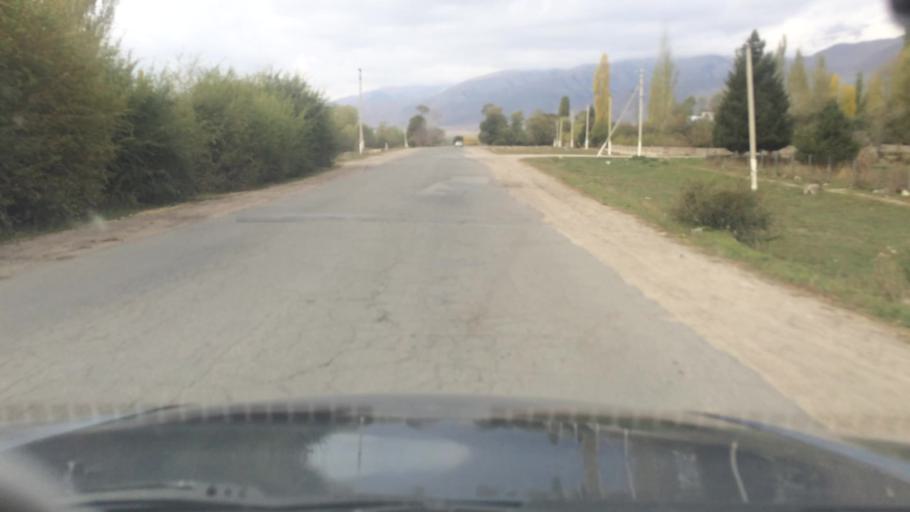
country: KG
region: Ysyk-Koel
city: Tyup
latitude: 42.7822
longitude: 78.2857
